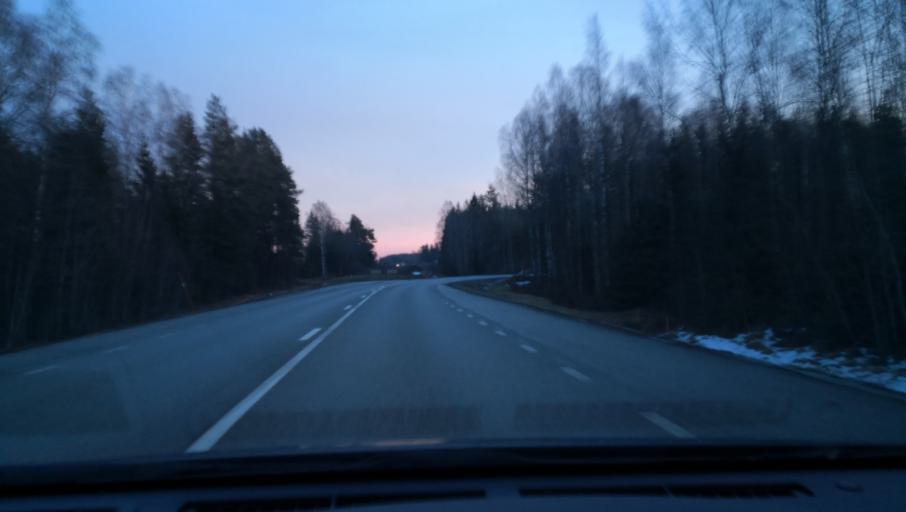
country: SE
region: OErebro
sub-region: Orebro Kommun
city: Orebro
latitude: 59.2411
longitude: 15.0989
